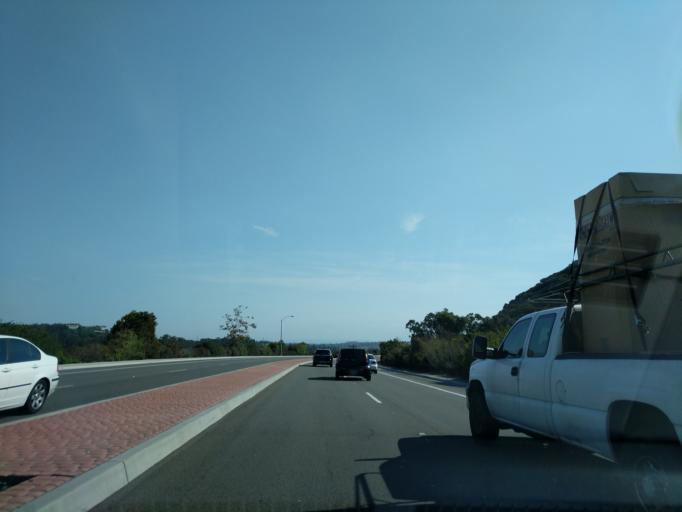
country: US
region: California
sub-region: San Diego County
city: Encinitas
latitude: 33.0859
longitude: -117.2940
